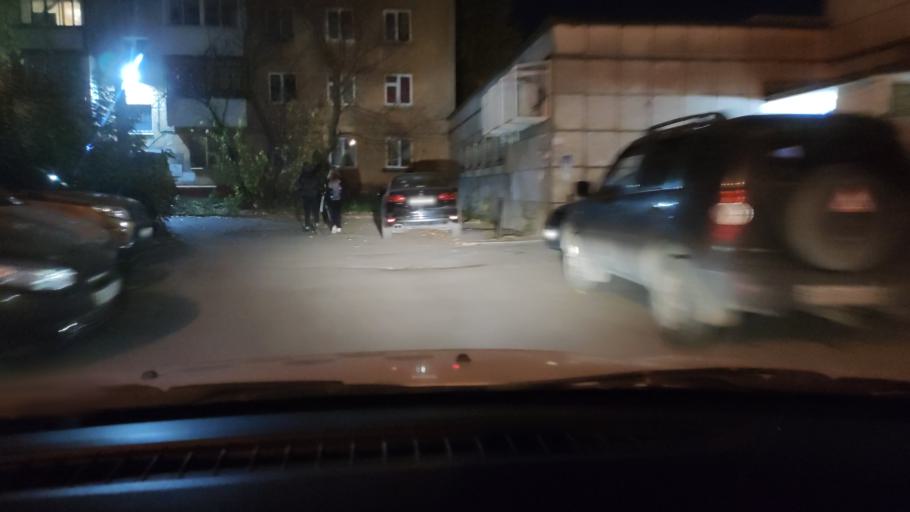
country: RU
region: Perm
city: Perm
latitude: 57.9980
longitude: 56.2956
